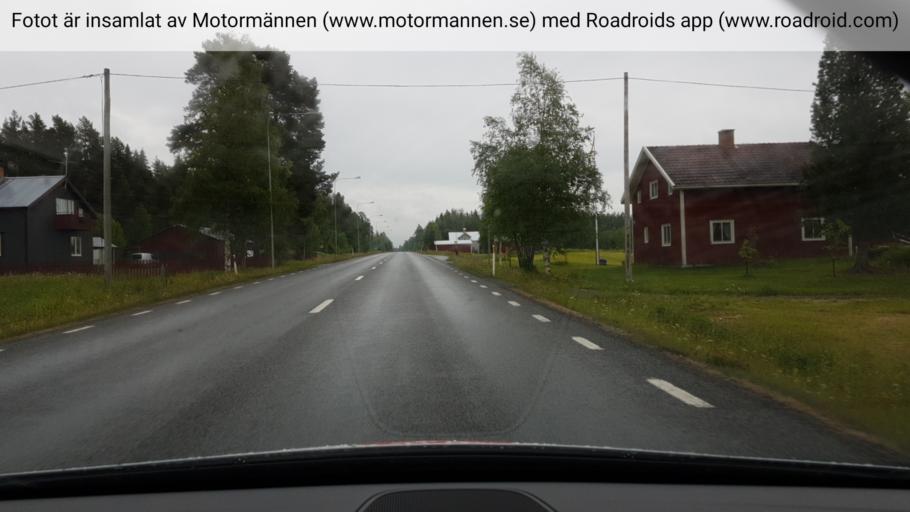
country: SE
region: Jaemtland
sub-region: OEstersunds Kommun
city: Lit
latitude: 63.3959
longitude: 15.0081
